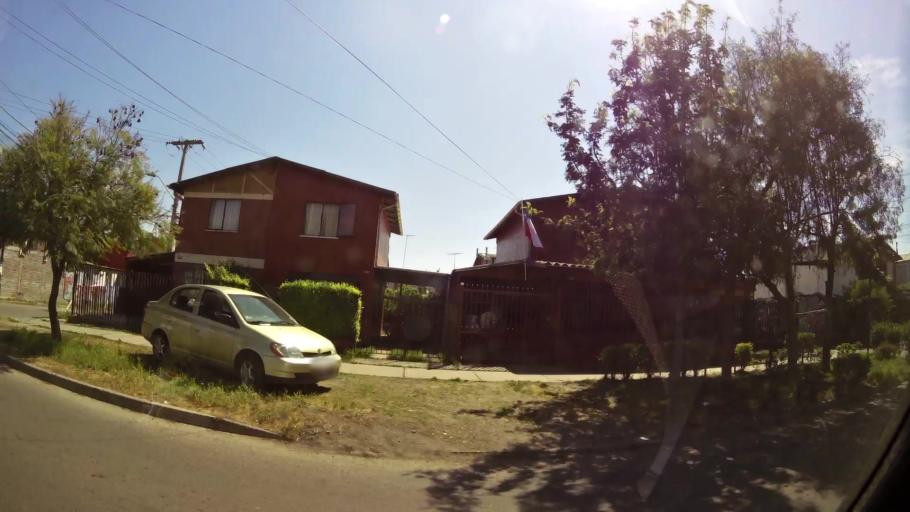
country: CL
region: Santiago Metropolitan
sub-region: Provincia de Talagante
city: Talagante
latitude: -33.6545
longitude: -70.9119
